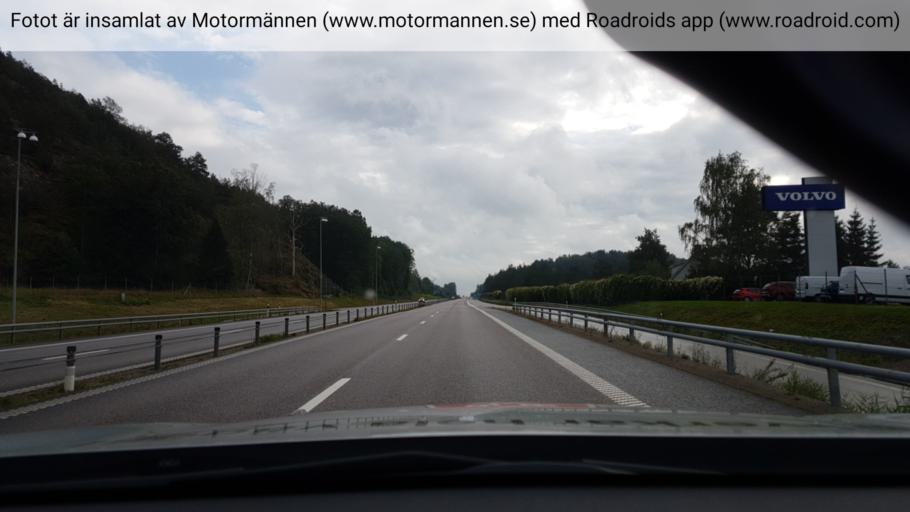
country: SE
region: Vaestra Goetaland
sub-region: Lilla Edets Kommun
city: Lilla Edet
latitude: 58.1436
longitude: 12.1351
